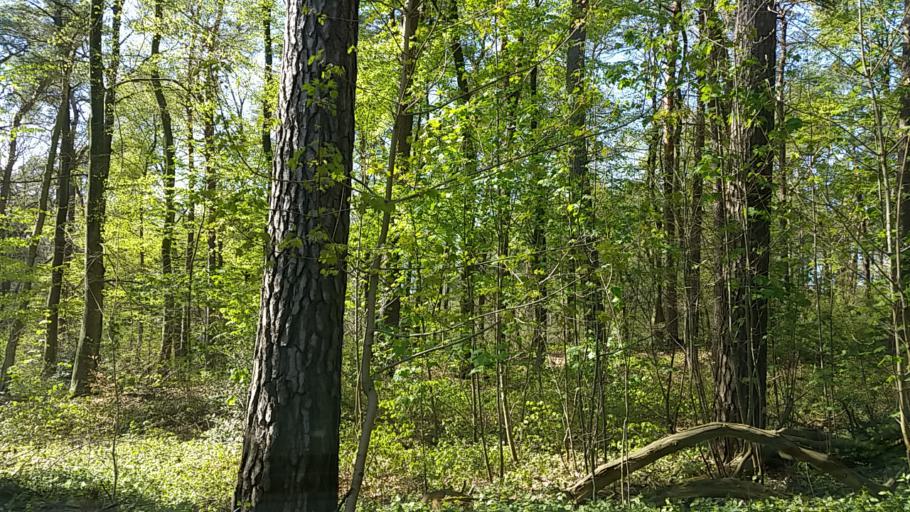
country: DE
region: Schleswig-Holstein
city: Wedel
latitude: 53.5915
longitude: 9.7532
